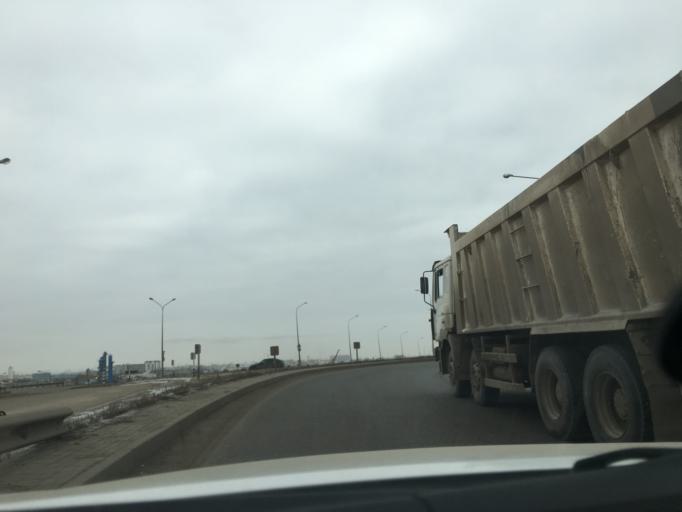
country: KZ
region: Astana Qalasy
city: Astana
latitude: 51.1540
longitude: 71.5332
